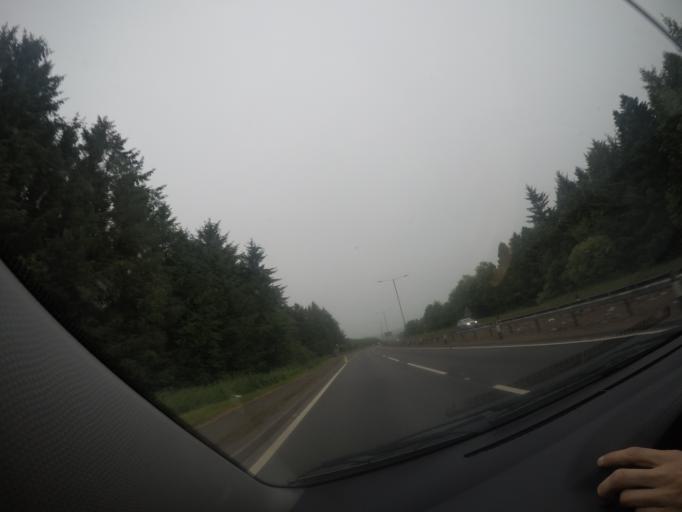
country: GB
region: Scotland
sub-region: Dundee City
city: Dundee
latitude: 56.5312
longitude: -2.9456
